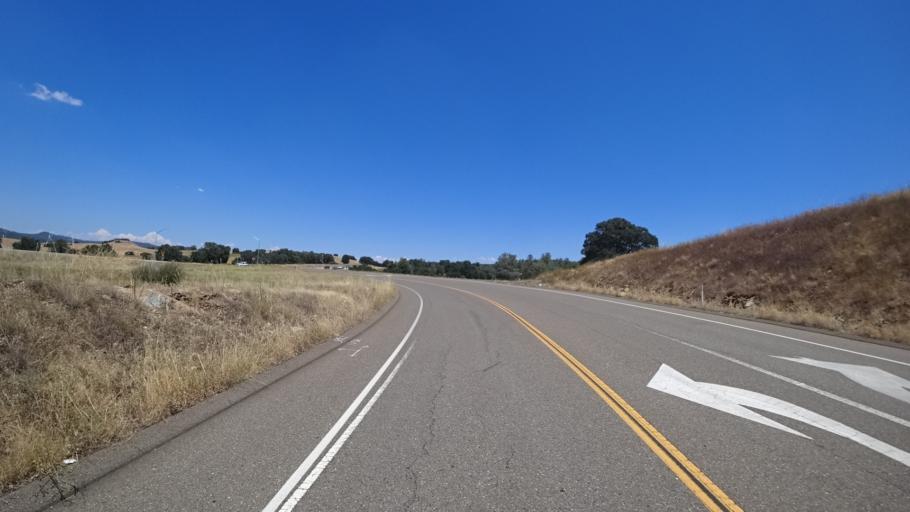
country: US
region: California
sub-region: Calaveras County
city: Angels Camp
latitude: 38.0784
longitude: -120.5277
